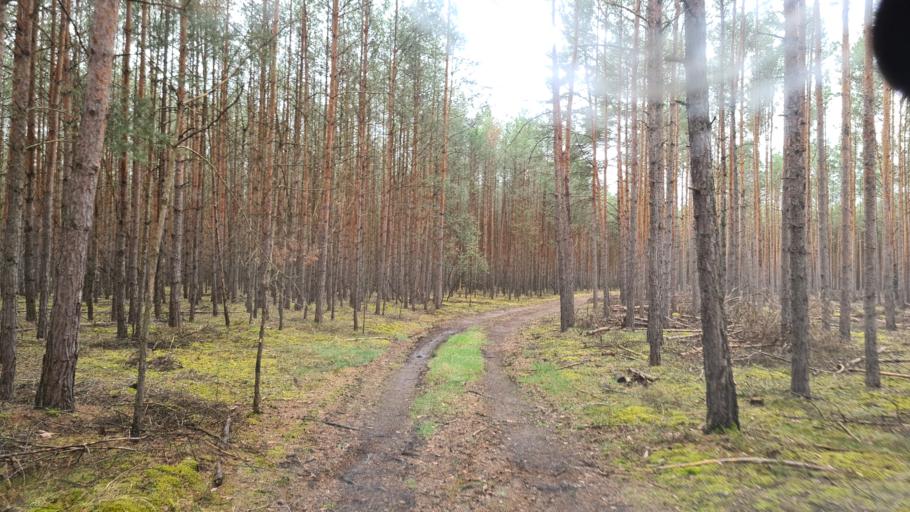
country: DE
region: Brandenburg
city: Schonewalde
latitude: 51.6468
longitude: 13.6301
